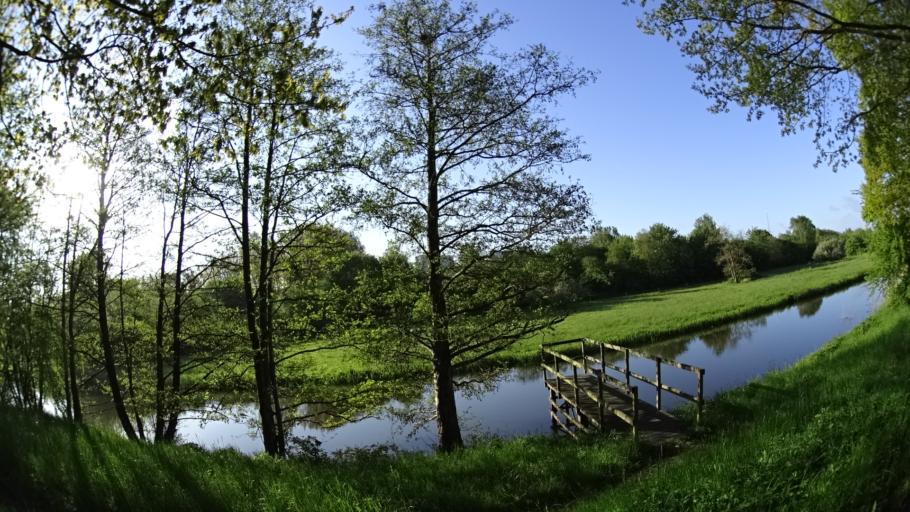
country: DK
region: Central Jutland
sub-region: Arhus Kommune
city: Arhus
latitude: 56.1484
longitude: 10.1762
